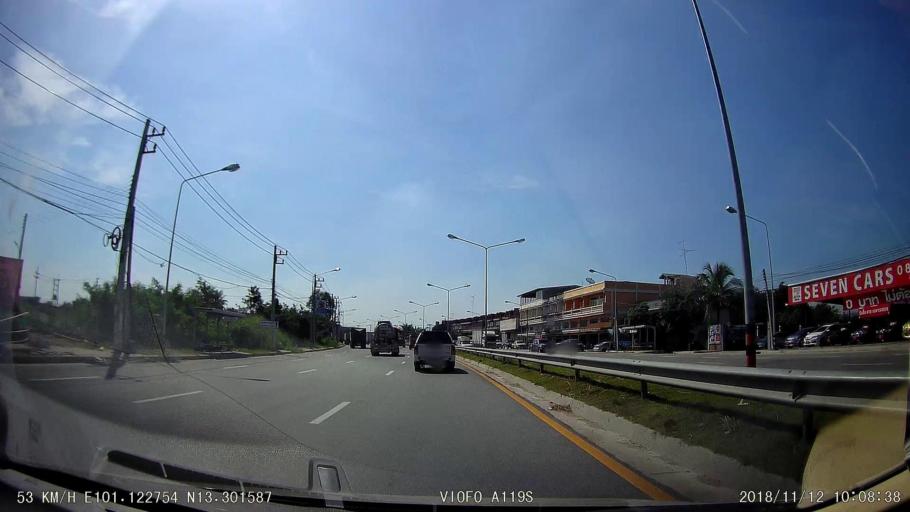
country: TH
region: Chon Buri
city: Ban Bueng
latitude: 13.3014
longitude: 101.1228
